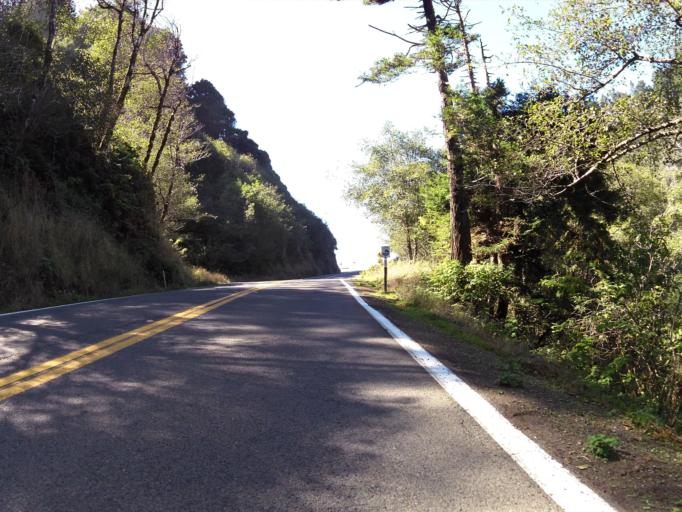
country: US
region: California
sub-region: Mendocino County
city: Fort Bragg
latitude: 39.7110
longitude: -123.8044
